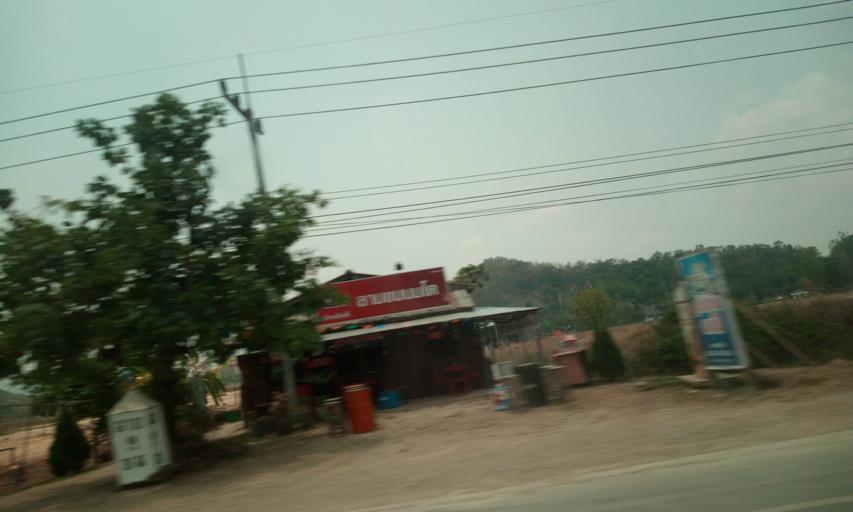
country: TH
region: Chiang Rai
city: Thoeng
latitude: 19.6905
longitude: 100.1484
